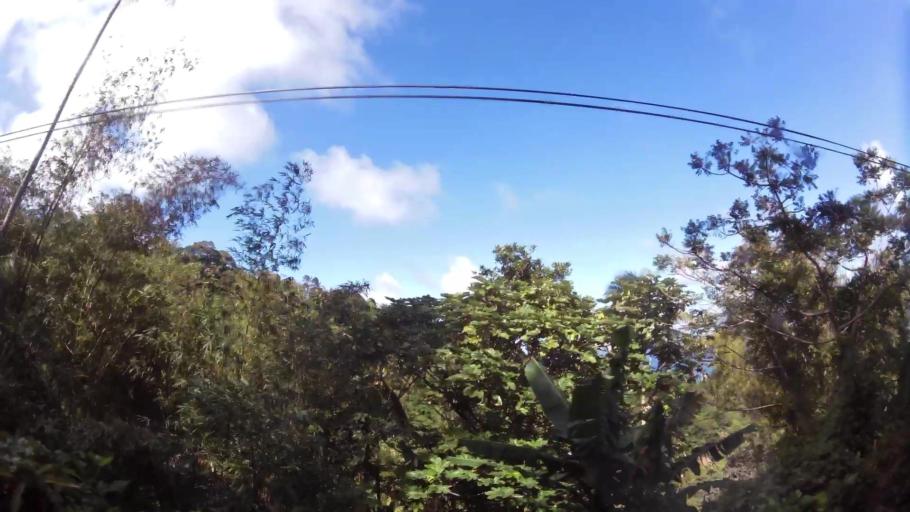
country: DM
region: Saint John
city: Portsmouth
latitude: 15.6261
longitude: -61.4199
